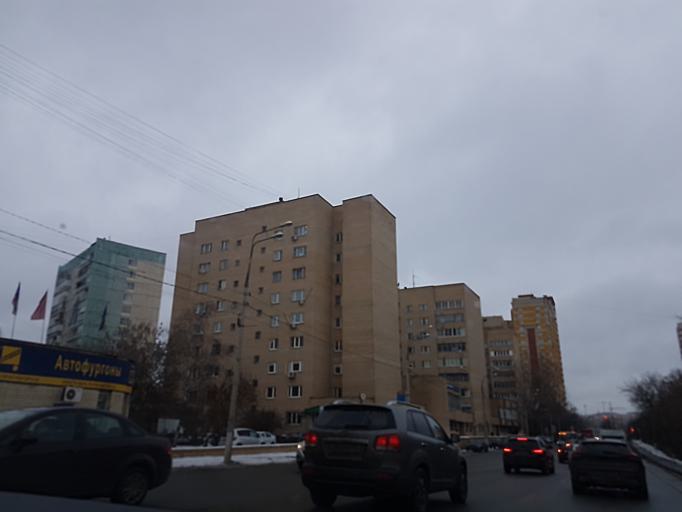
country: RU
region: Moskovskaya
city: Pavshino
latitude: 55.8138
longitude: 37.3471
